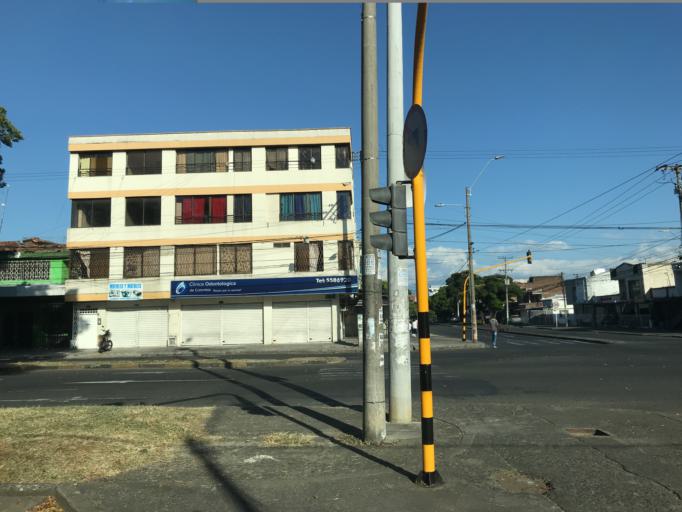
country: CO
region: Valle del Cauca
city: Cali
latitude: 3.4361
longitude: -76.5282
